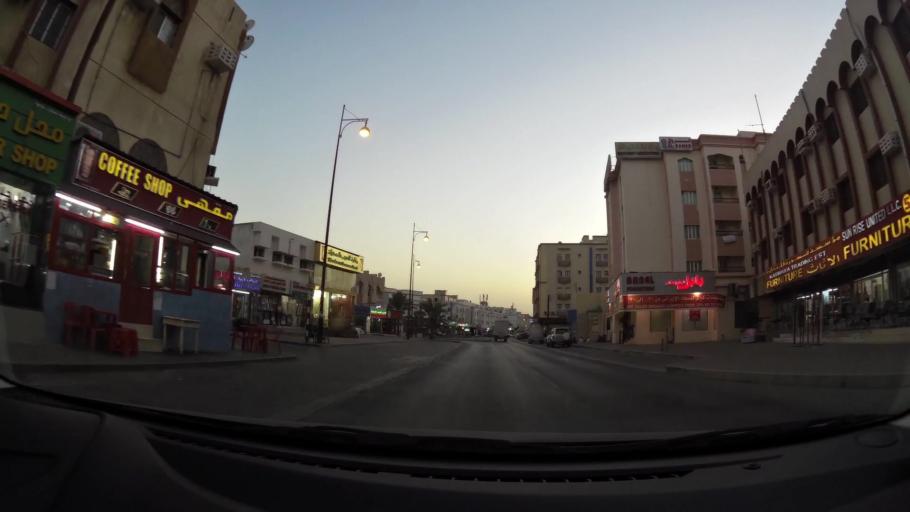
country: OM
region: Muhafazat Masqat
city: As Sib al Jadidah
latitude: 23.6837
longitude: 58.1783
